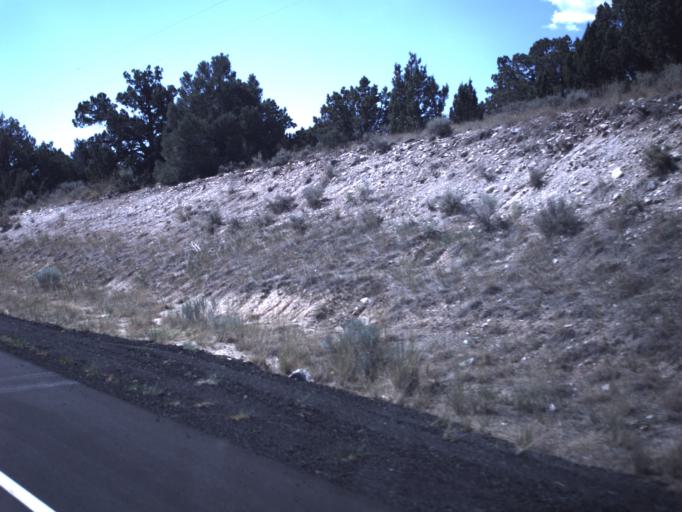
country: US
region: Utah
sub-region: Utah County
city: Eagle Mountain
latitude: 40.0318
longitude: -112.2846
